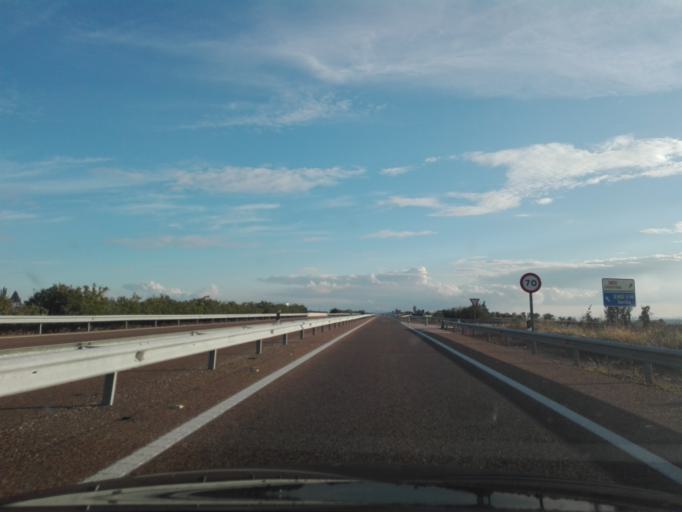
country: ES
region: Extremadura
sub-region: Provincia de Badajoz
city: Puebla de Sancho Perez
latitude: 38.3982
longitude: -6.3406
